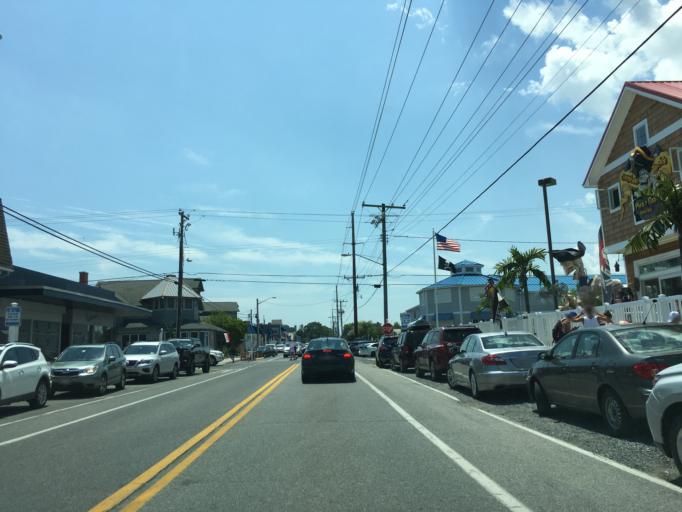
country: US
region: Delaware
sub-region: Sussex County
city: Bethany Beach
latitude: 38.5407
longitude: -75.0575
